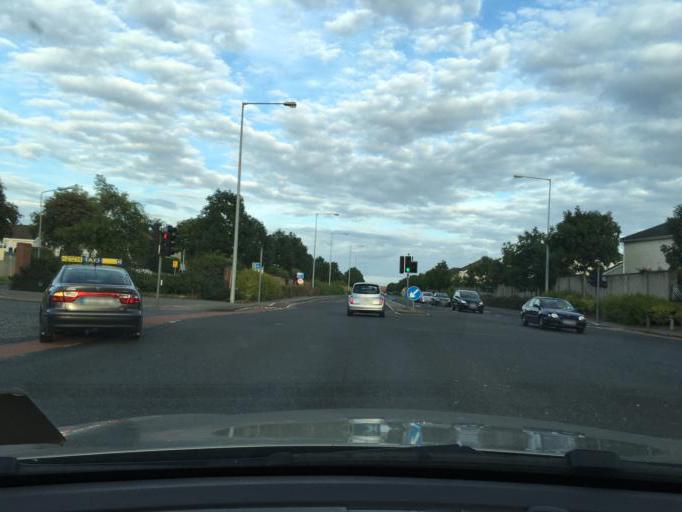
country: IE
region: Leinster
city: Hartstown
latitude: 53.3871
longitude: -6.4103
